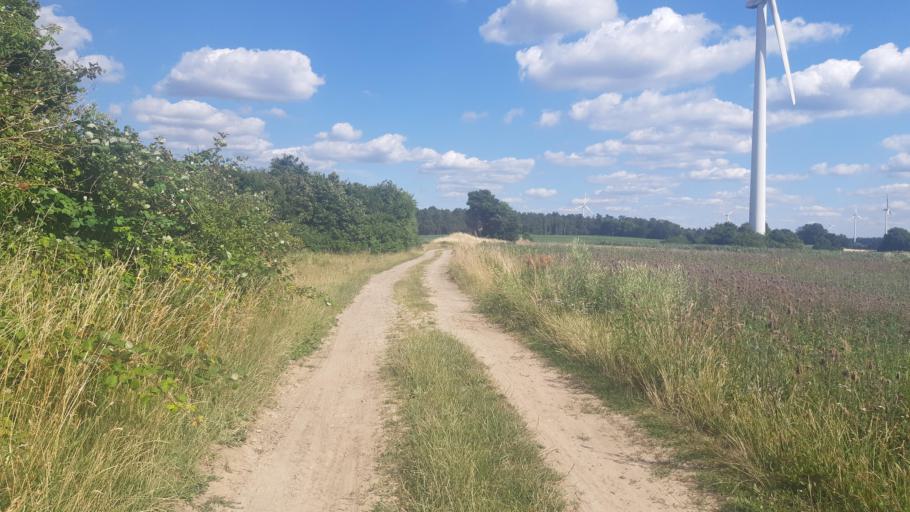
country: DE
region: Lower Saxony
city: Dahlem
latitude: 53.2061
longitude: 10.7565
